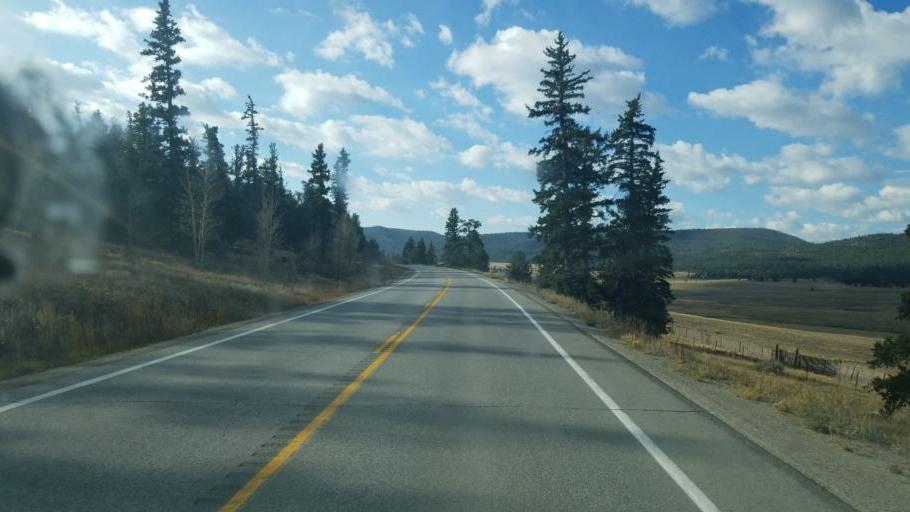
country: US
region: Colorado
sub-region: Chaffee County
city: Buena Vista
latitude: 38.8985
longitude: -105.9906
